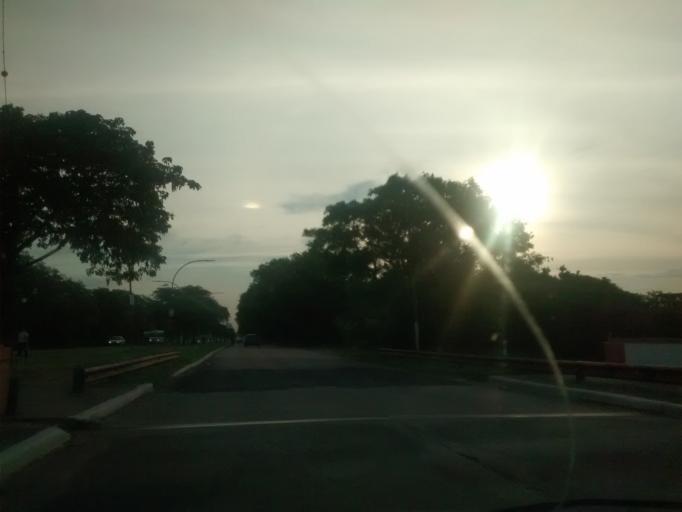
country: AR
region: Chaco
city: Resistencia
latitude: -27.4295
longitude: -58.9625
